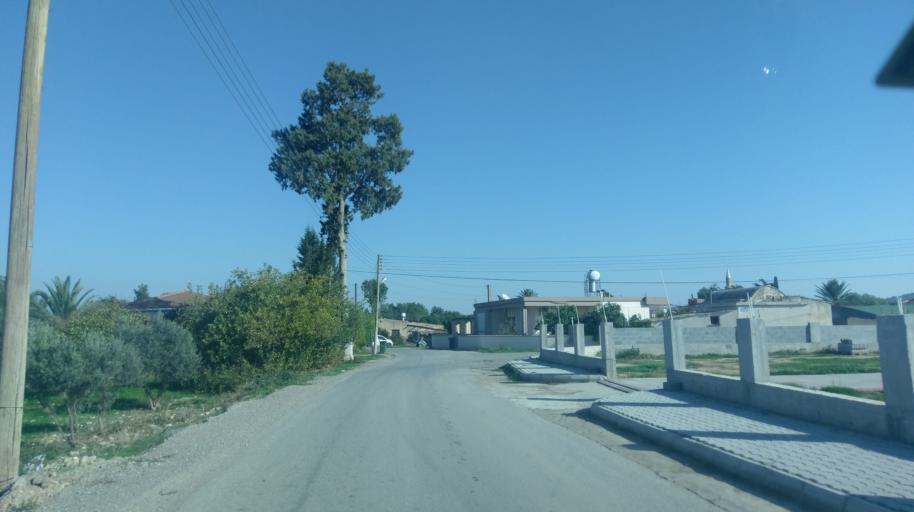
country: CY
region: Larnaka
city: Troulloi
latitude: 35.0847
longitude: 33.6065
